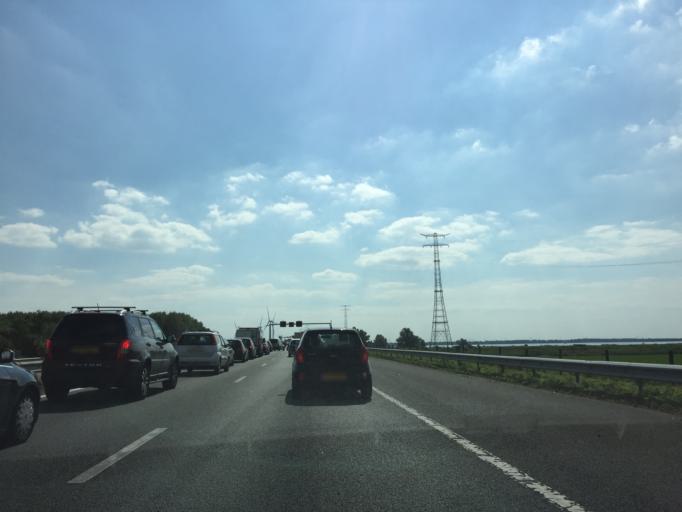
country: NL
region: North Brabant
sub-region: Gemeente Moerdijk
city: Willemstad
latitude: 51.7268
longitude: 4.4075
